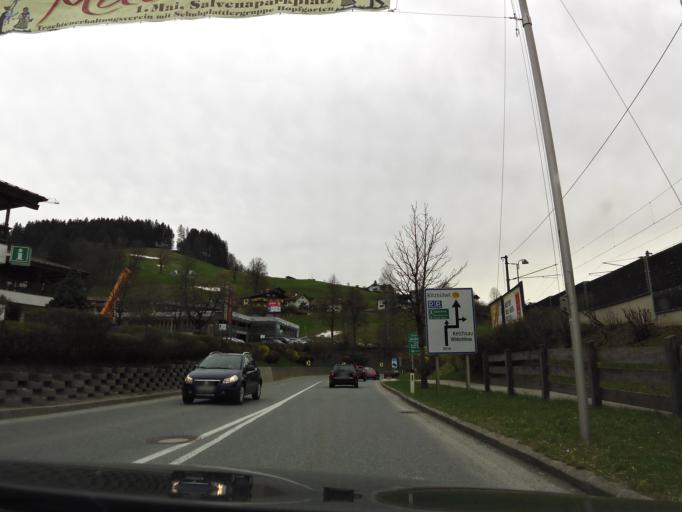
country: AT
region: Tyrol
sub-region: Politischer Bezirk Kitzbuhel
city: Hopfgarten im Brixental
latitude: 47.4469
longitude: 12.1590
